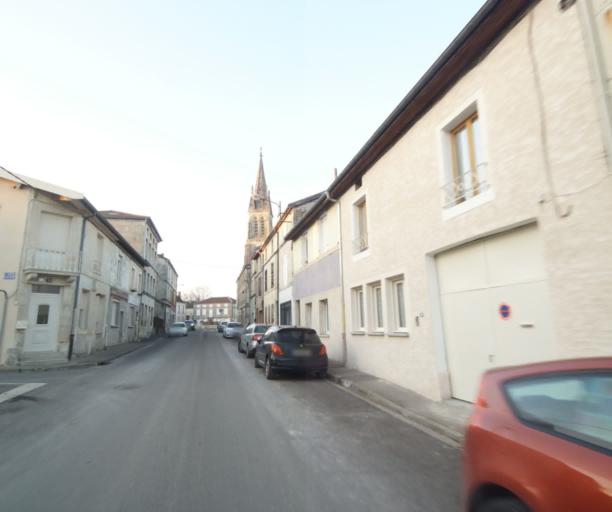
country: FR
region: Champagne-Ardenne
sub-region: Departement de la Haute-Marne
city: Bienville
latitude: 48.5845
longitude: 5.0381
